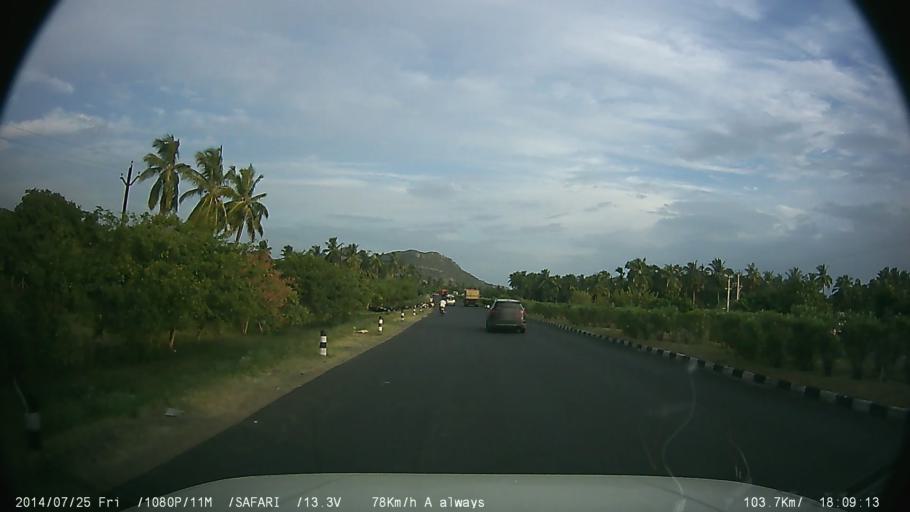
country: IN
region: Tamil Nadu
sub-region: Krishnagiri
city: Kaverippattanam
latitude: 12.3915
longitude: 78.2189
